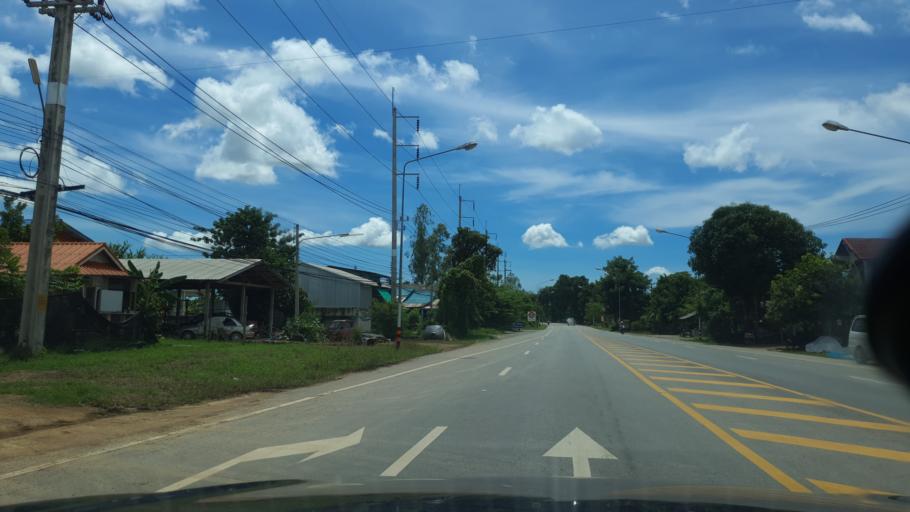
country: TH
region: Sukhothai
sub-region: Amphoe Si Satchanalai
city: Si Satchanalai
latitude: 17.5079
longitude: 99.7582
